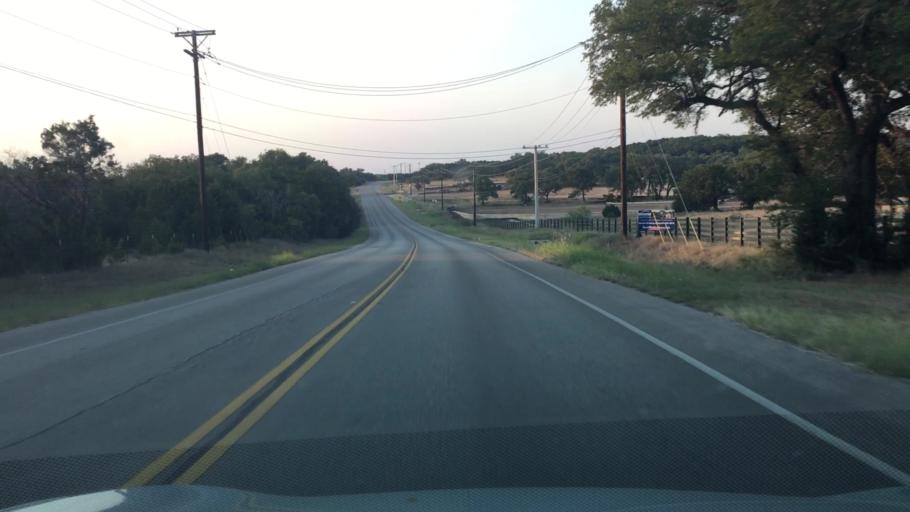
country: US
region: Texas
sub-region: Hays County
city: Dripping Springs
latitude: 30.1610
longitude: -98.0086
